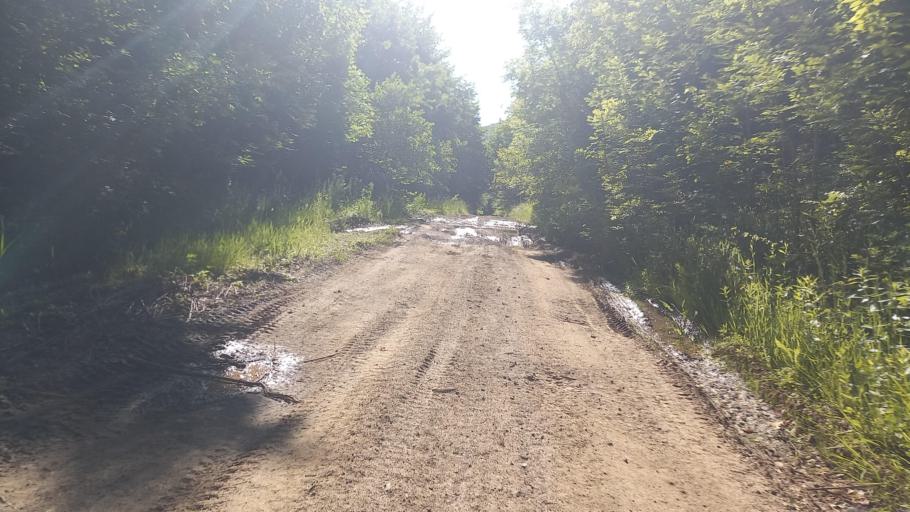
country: RU
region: Krasnodarskiy
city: Dzhubga
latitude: 44.5371
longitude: 38.7521
